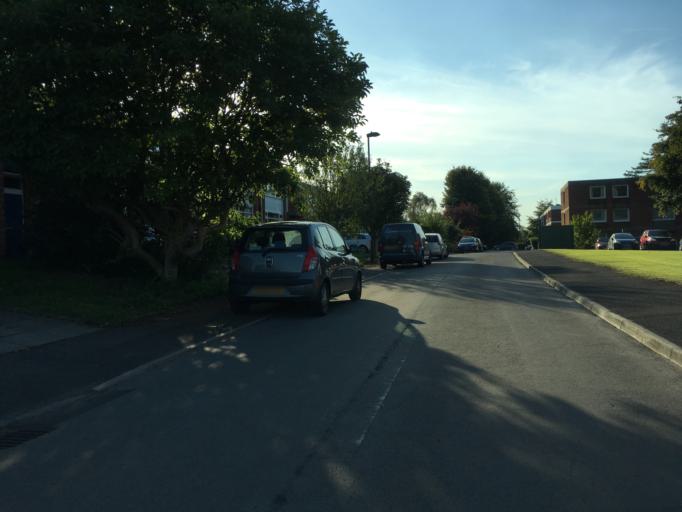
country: GB
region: England
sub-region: South Gloucestershire
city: Mangotsfield
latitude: 51.5017
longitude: -2.5203
